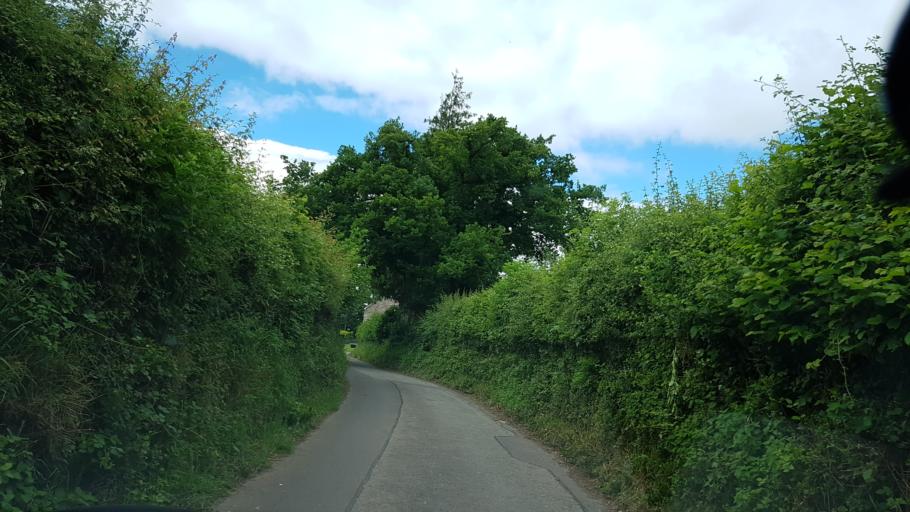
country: GB
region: Wales
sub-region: Monmouthshire
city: Llanarth
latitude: 51.8276
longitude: -2.8783
